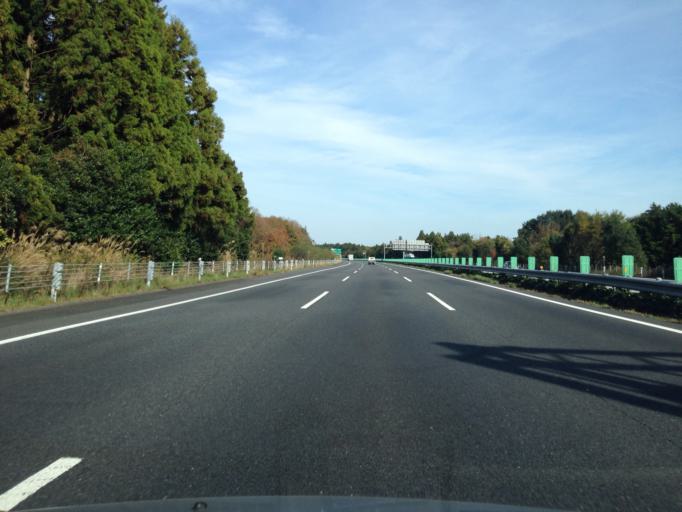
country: JP
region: Ibaraki
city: Tomobe
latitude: 36.3290
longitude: 140.3538
